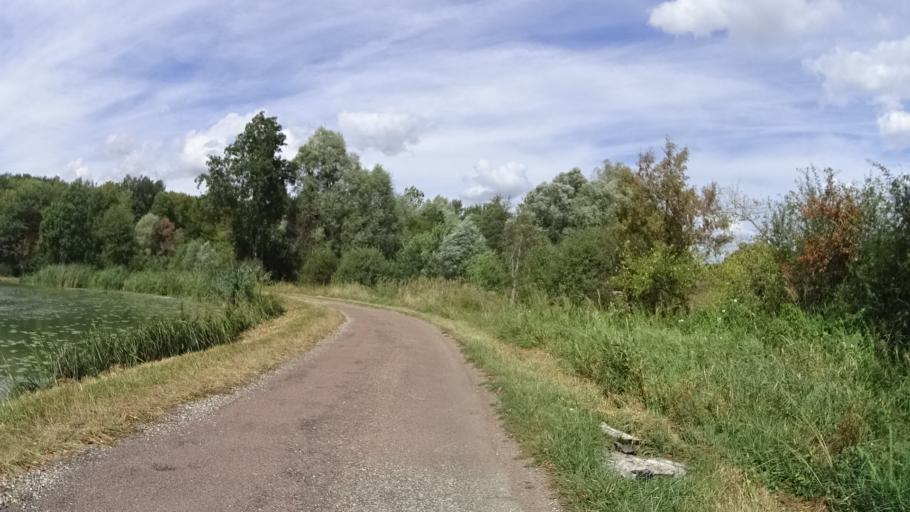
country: FR
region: Bourgogne
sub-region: Departement de la Cote-d'Or
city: Saint-Jean-de-Losne
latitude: 47.0960
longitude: 5.3255
